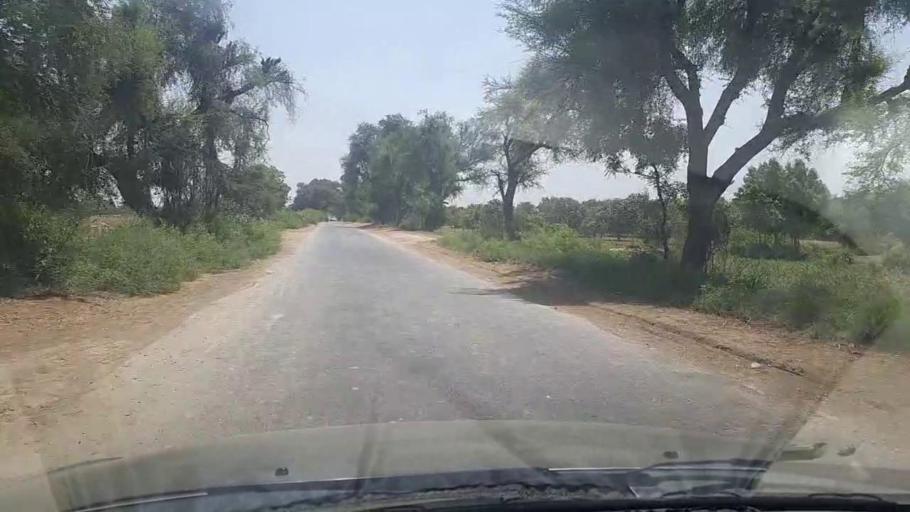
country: PK
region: Sindh
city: Tando Jam
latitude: 25.2811
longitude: 68.6074
